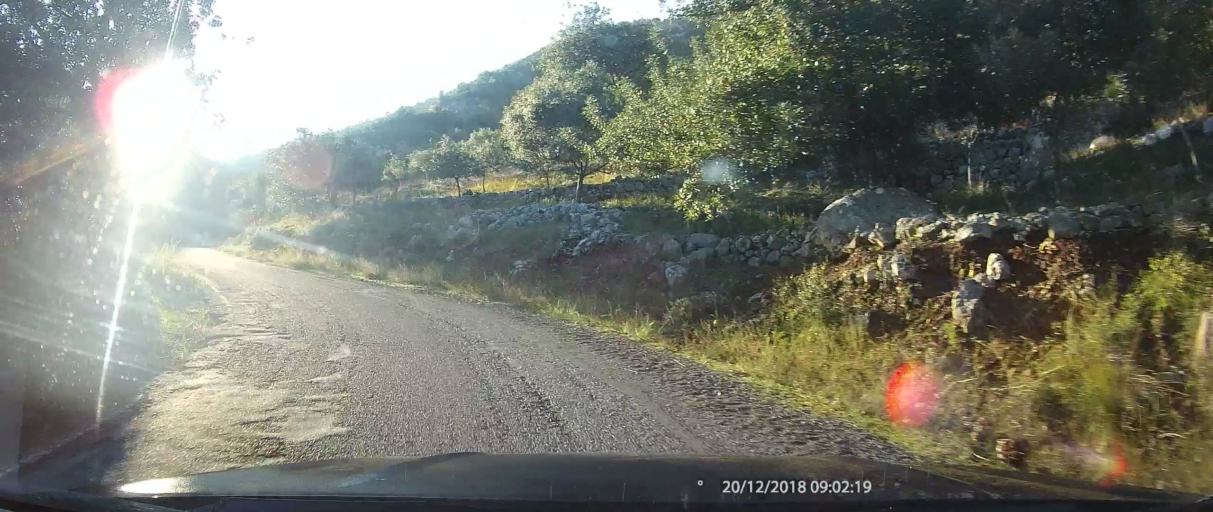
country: GR
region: Peloponnese
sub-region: Nomos Lakonias
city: Sykea
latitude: 36.9549
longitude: 22.9917
